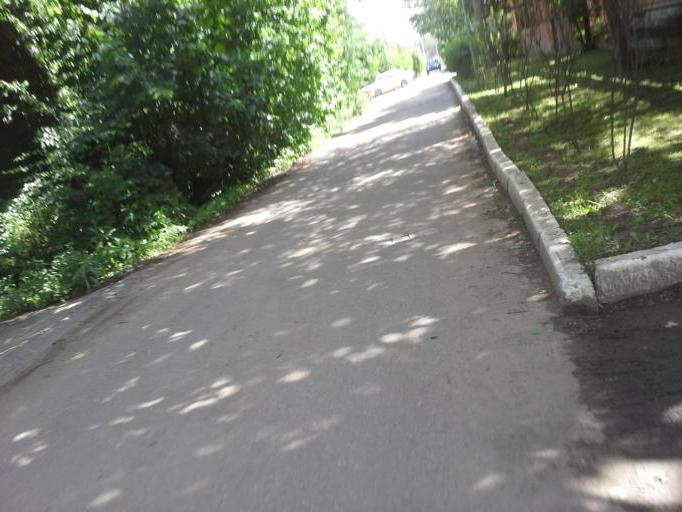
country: RU
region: Moskovskaya
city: Lesnoy Gorodok
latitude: 55.6293
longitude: 37.2151
